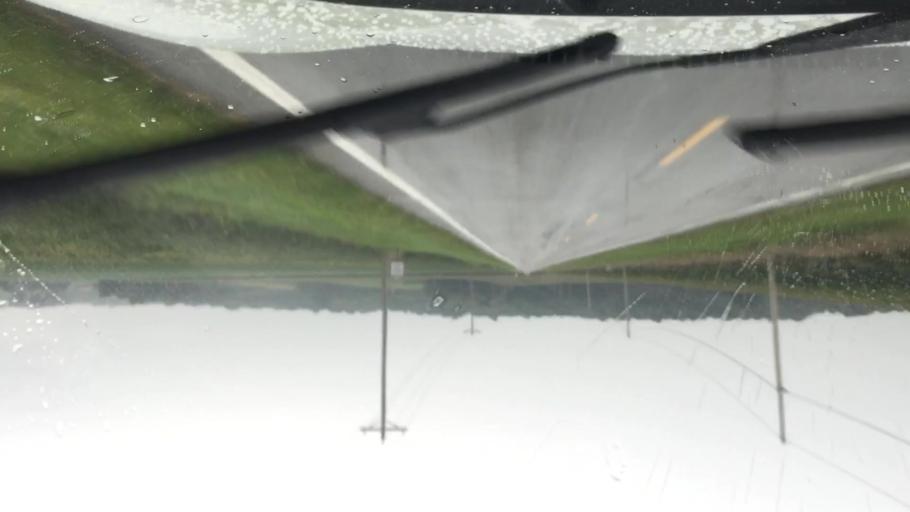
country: US
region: Ohio
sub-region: Champaign County
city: Mechanicsburg
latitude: 40.0289
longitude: -83.6467
